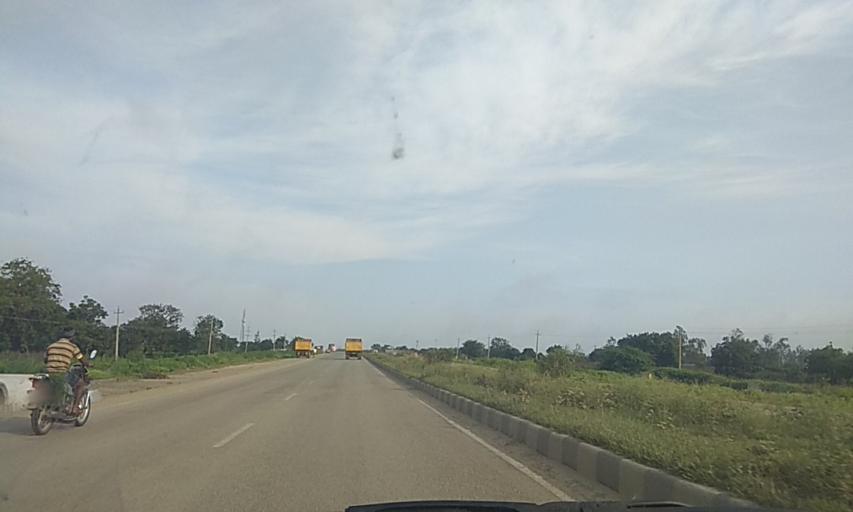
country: IN
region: Karnataka
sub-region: Haveri
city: Byadgi
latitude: 14.6991
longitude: 75.5247
